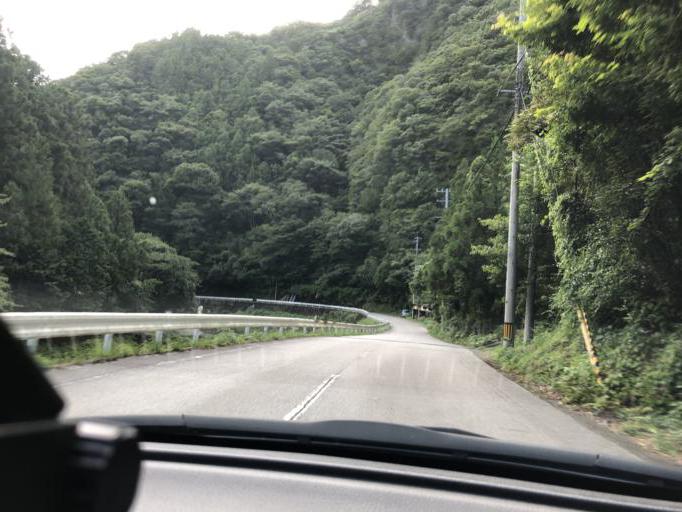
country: JP
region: Kochi
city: Kochi-shi
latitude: 33.6279
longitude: 133.5054
